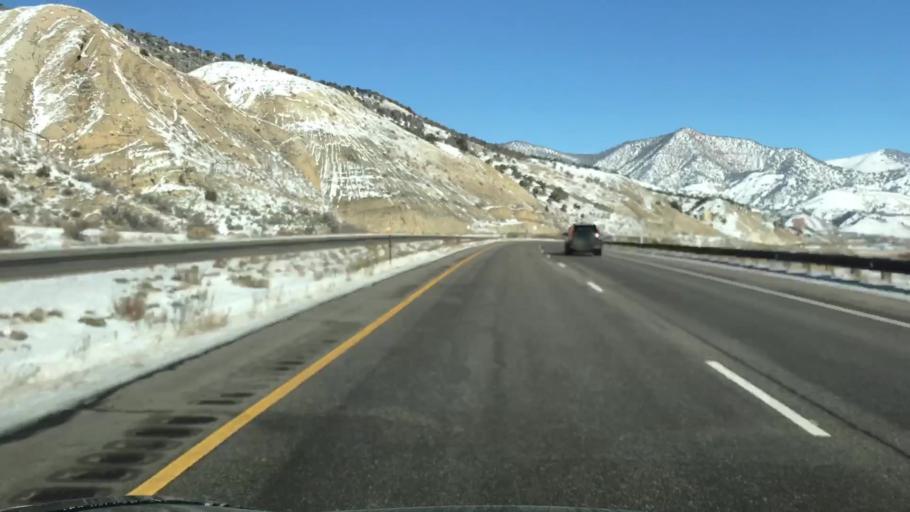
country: US
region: Colorado
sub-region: Eagle County
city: Gypsum
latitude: 39.6435
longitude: -107.0808
